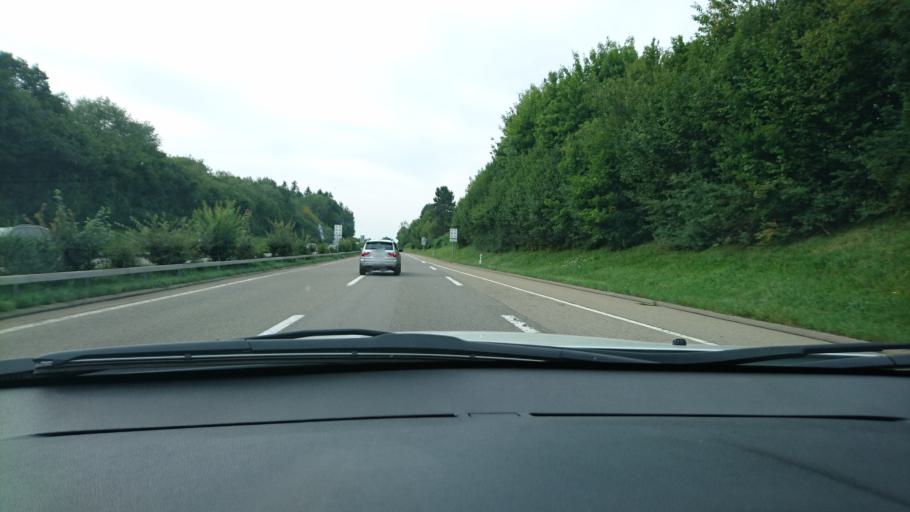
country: CH
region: Zurich
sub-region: Bezirk Hinwil
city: Durnten
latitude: 47.2775
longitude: 8.8279
